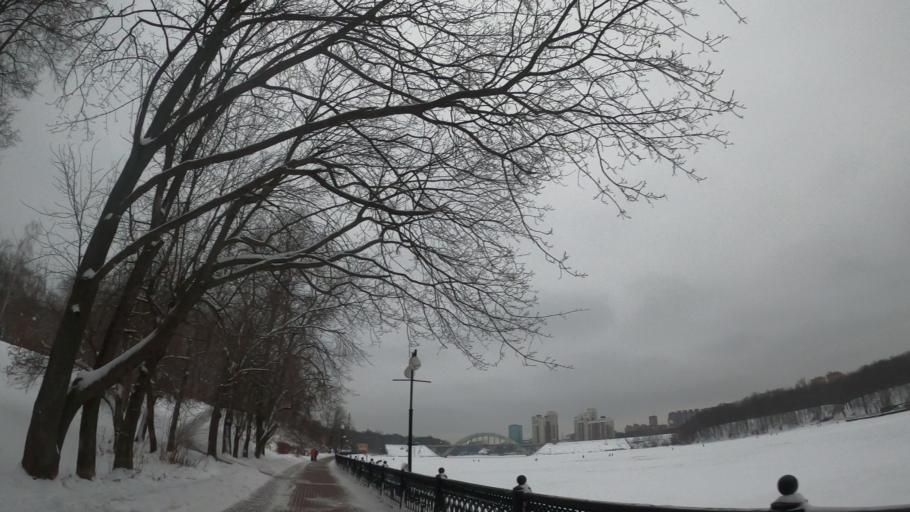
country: RU
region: Moskovskaya
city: Levoberezhnaya
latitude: 55.8946
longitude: 37.4687
